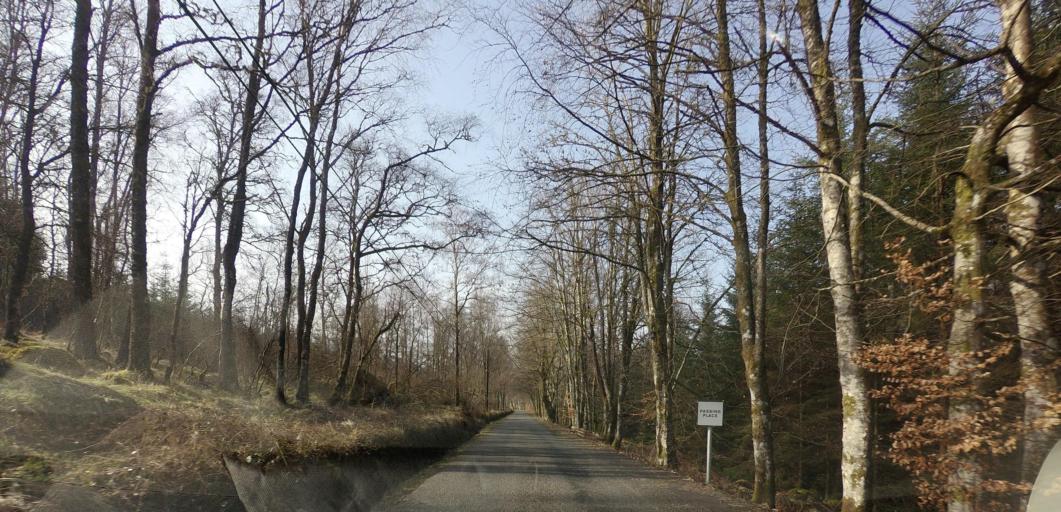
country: GB
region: Scotland
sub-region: Stirling
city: Callander
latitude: 56.4642
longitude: -4.2931
